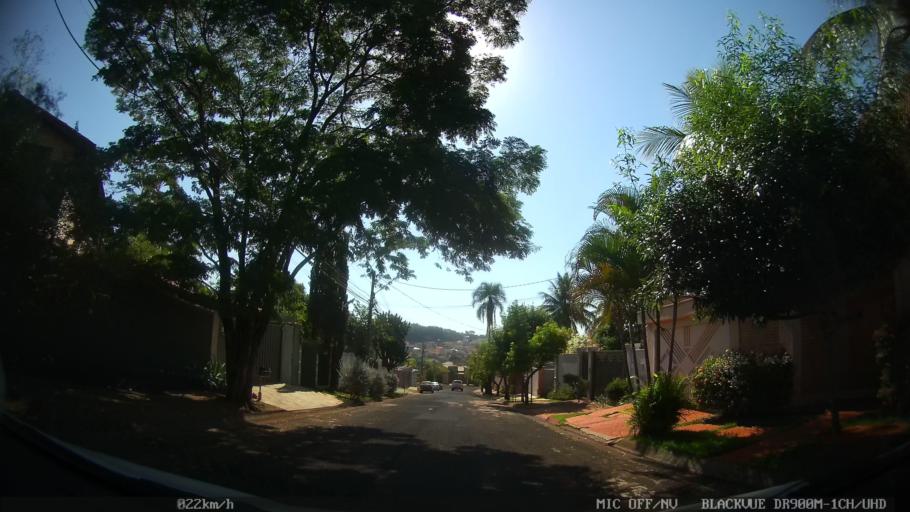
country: BR
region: Sao Paulo
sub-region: Ribeirao Preto
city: Ribeirao Preto
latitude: -21.2130
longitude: -47.7877
